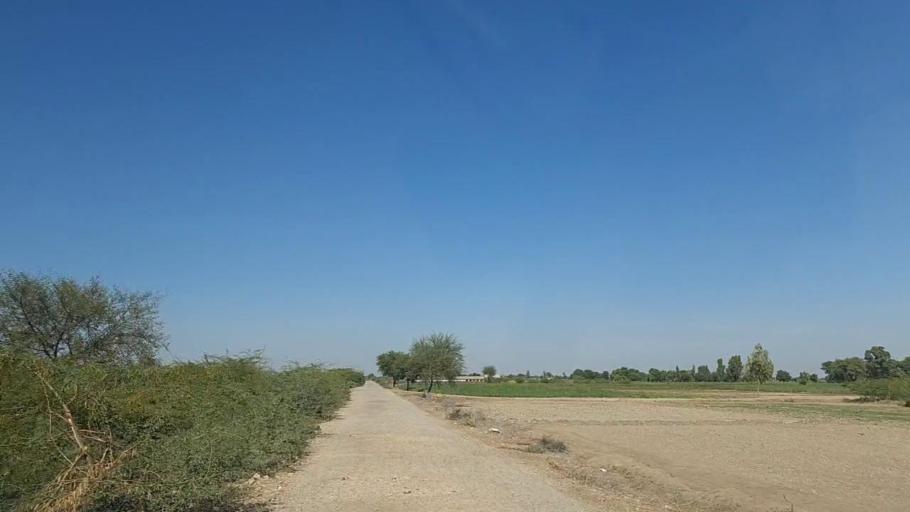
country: PK
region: Sindh
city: Samaro
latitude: 25.3033
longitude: 69.5148
